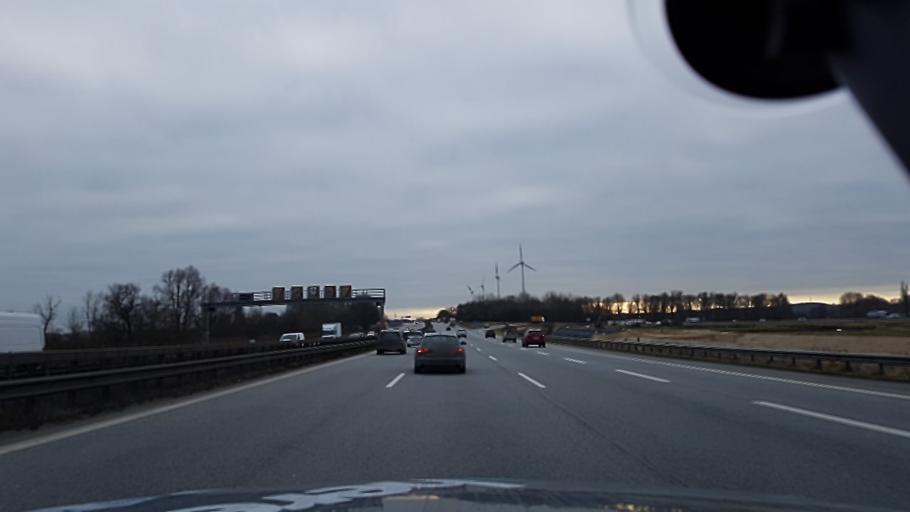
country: DE
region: Hamburg
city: Harburg
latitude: 53.4681
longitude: 10.0242
